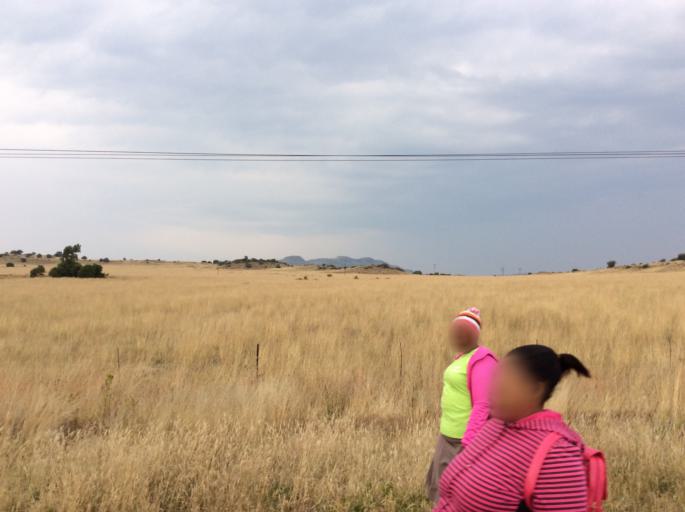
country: LS
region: Mafeteng
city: Mafeteng
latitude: -29.9873
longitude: 27.0267
